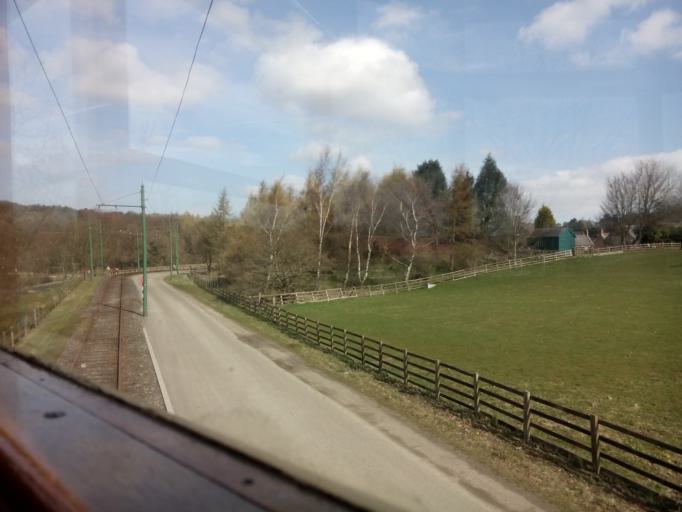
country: GB
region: England
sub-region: County Durham
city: Stanley
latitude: 54.8879
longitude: -1.6622
